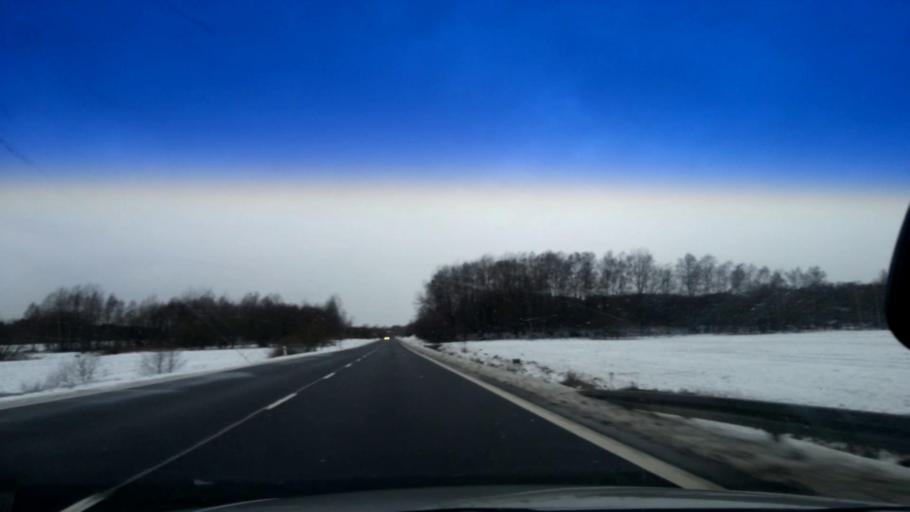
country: CZ
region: Karlovarsky
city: As
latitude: 50.1995
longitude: 12.2009
